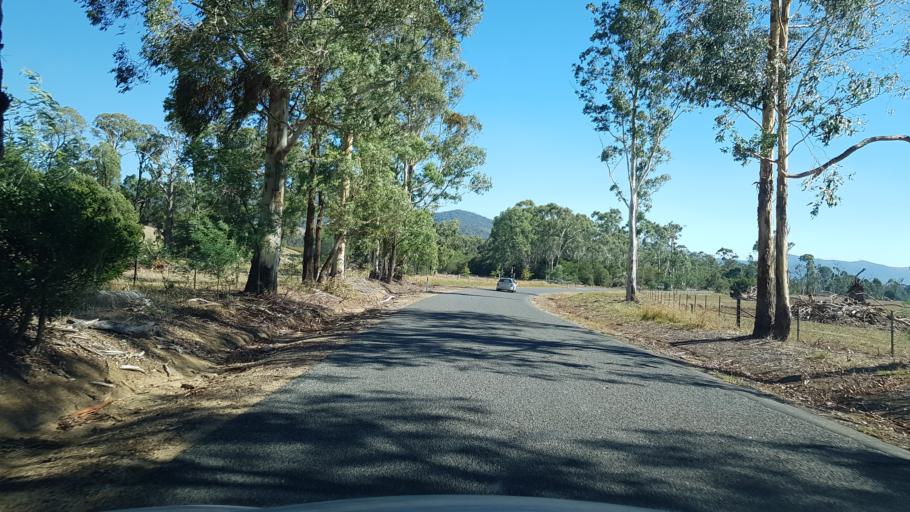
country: AU
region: Victoria
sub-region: Mansfield
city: Mansfield
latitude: -36.8106
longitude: 146.4414
